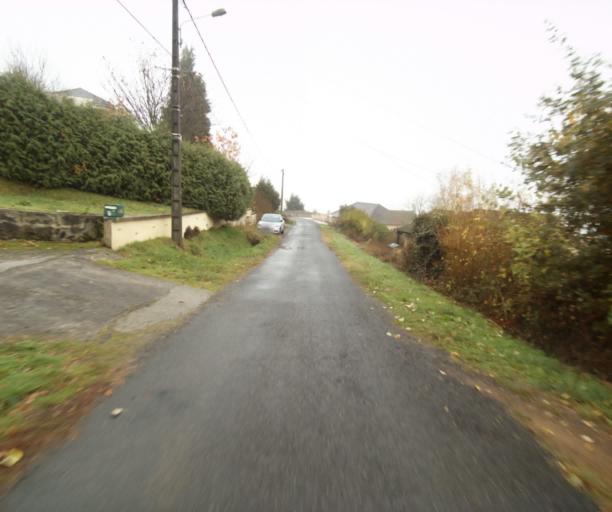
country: FR
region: Limousin
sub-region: Departement de la Correze
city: Sainte-Fereole
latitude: 45.1849
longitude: 1.6194
